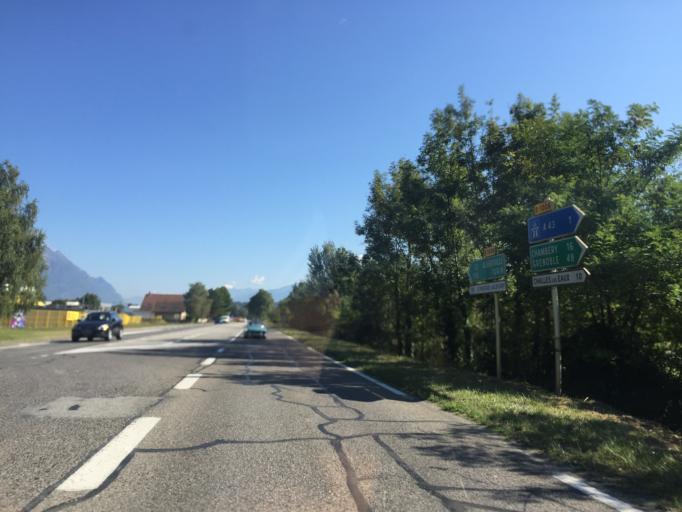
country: FR
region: Rhone-Alpes
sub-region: Departement de la Savoie
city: Montmelian
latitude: 45.5019
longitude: 6.0677
